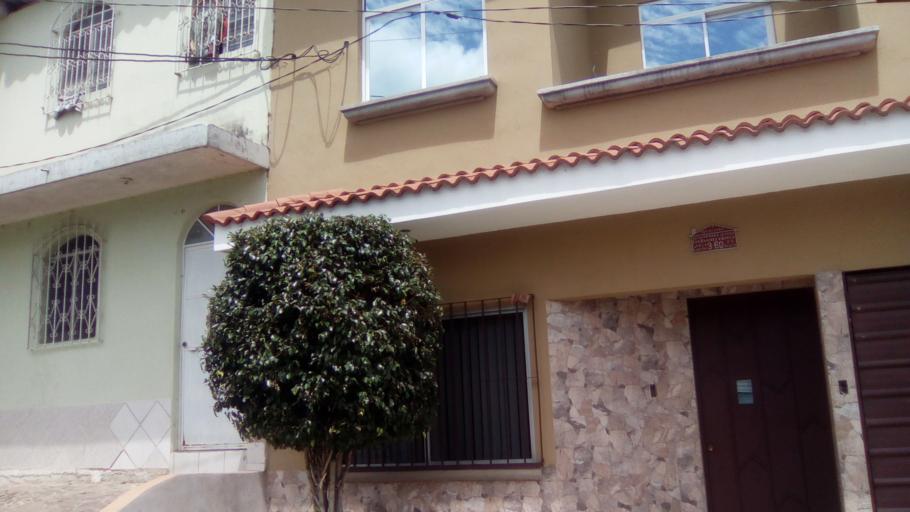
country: GT
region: Guatemala
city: Mixco
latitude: 14.5852
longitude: -90.6044
